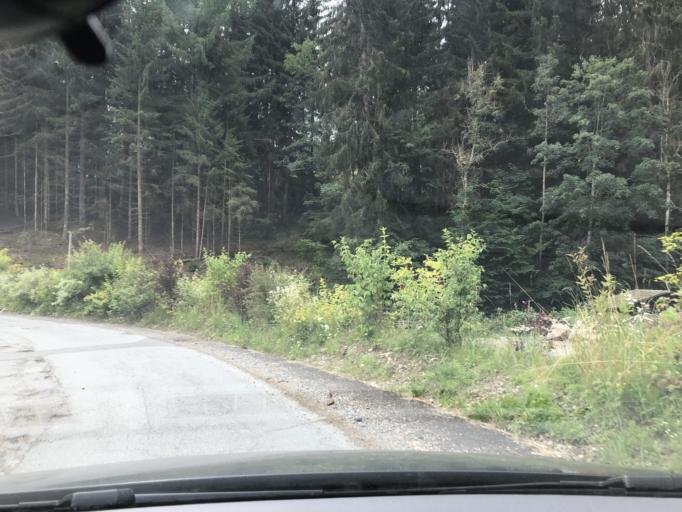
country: FR
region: Rhone-Alpes
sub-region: Departement de la Haute-Savoie
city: Combloux
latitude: 45.9010
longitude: 6.6268
